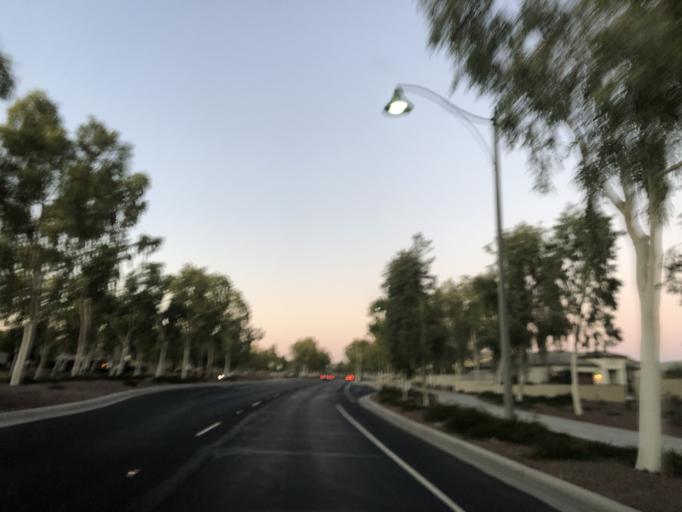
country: US
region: Arizona
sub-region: Maricopa County
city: Citrus Park
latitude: 33.4712
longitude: -112.5042
